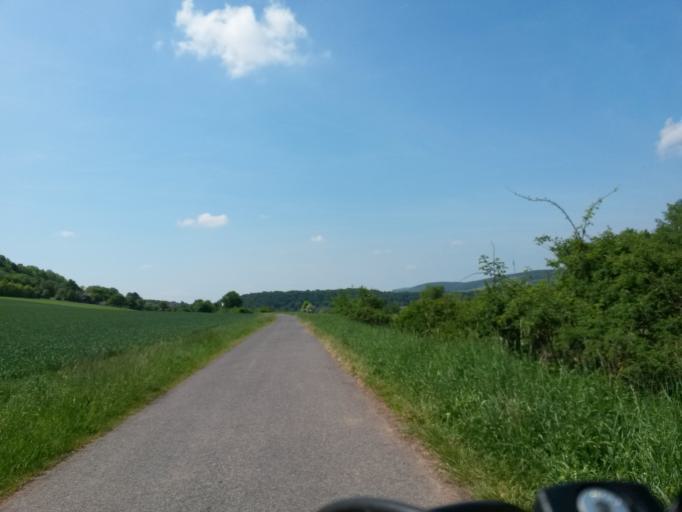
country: DE
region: Bavaria
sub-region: Regierungsbezirk Unterfranken
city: Elfershausen
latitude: 50.1406
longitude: 9.9853
